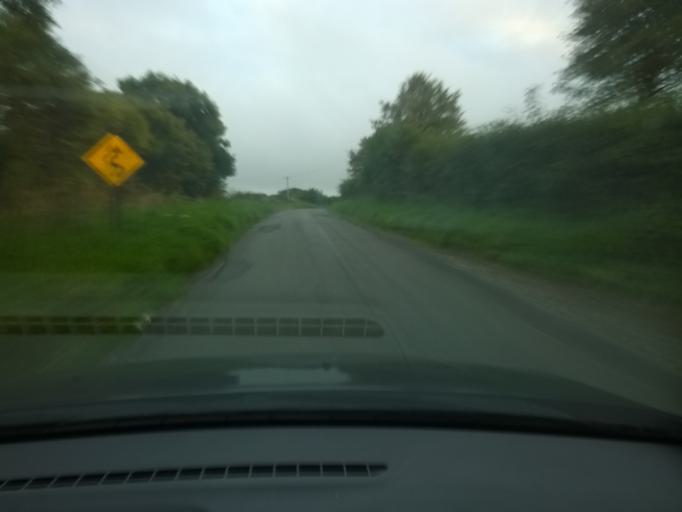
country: IE
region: Leinster
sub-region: Kildare
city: Kildare
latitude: 53.1715
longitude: -6.9295
